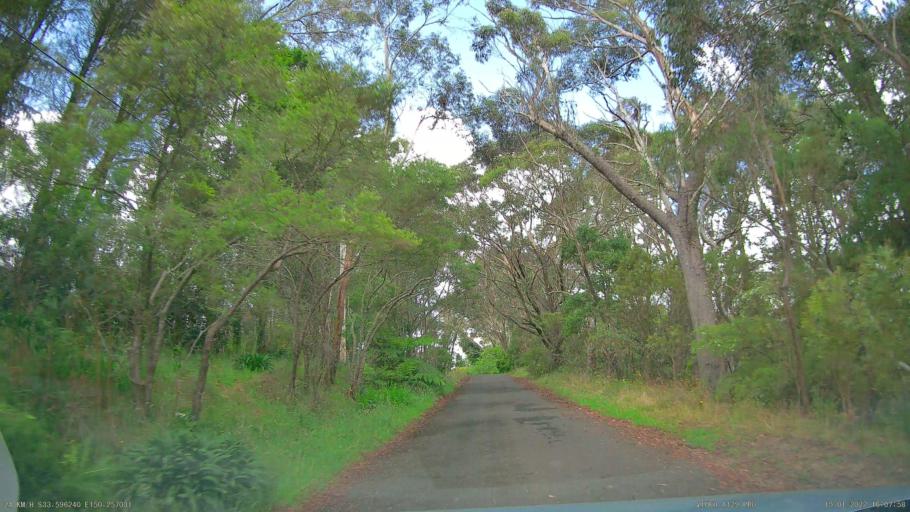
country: AU
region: New South Wales
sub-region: Blue Mountains Municipality
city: Blackheath
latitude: -33.5962
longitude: 150.2571
